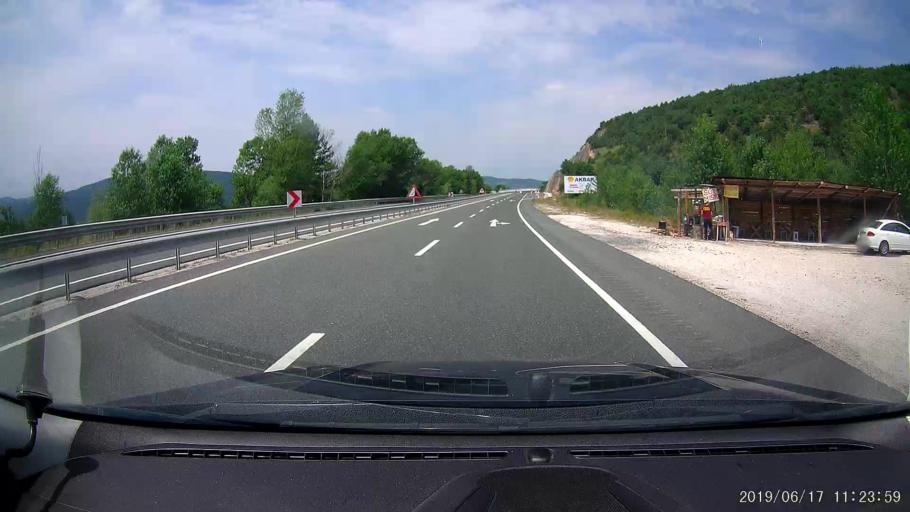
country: TR
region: Cankiri
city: Ilgaz
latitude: 40.8839
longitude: 33.7171
